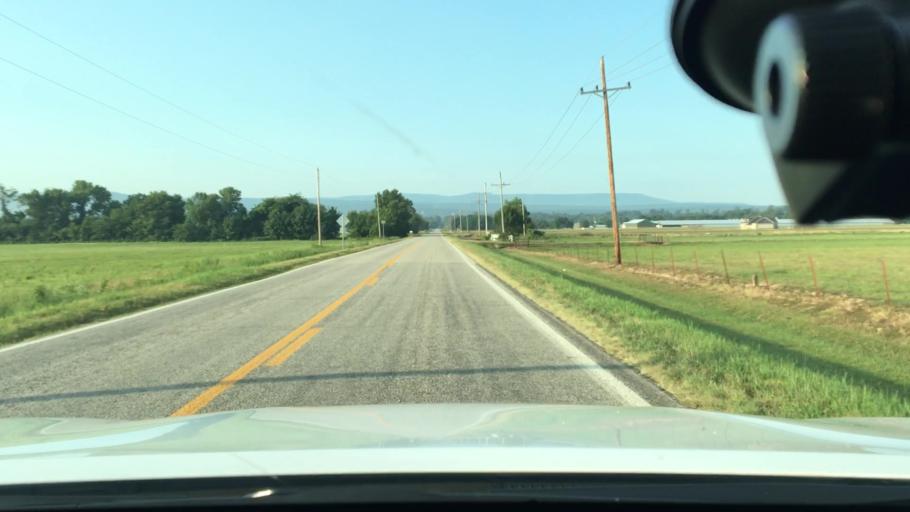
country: US
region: Arkansas
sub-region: Logan County
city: Paris
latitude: 35.3353
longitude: -93.6319
